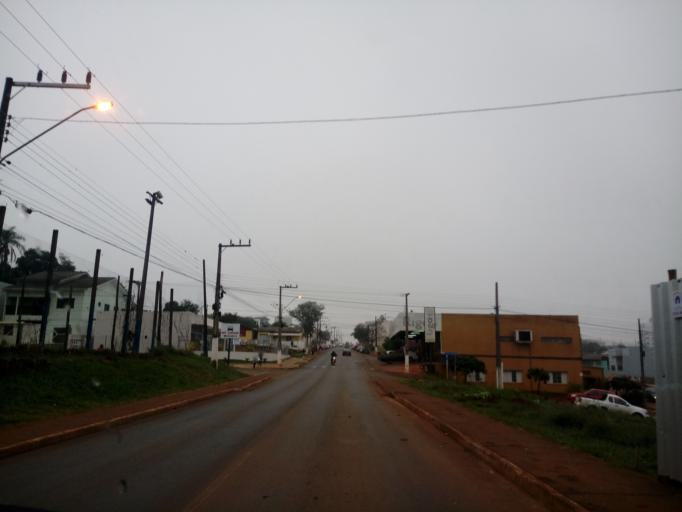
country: BR
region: Santa Catarina
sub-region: Chapeco
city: Chapeco
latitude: -27.1026
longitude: -52.6735
